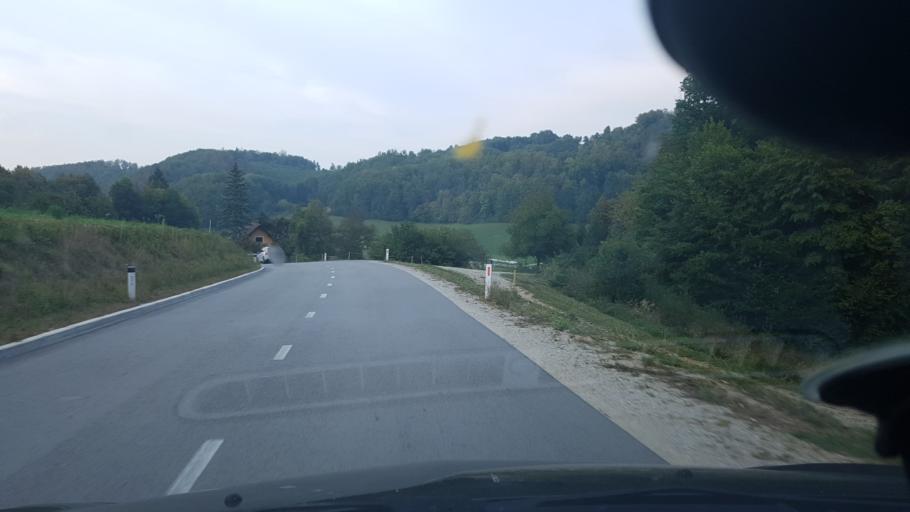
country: SI
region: Kozje
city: Kozje
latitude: 46.0756
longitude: 15.5697
